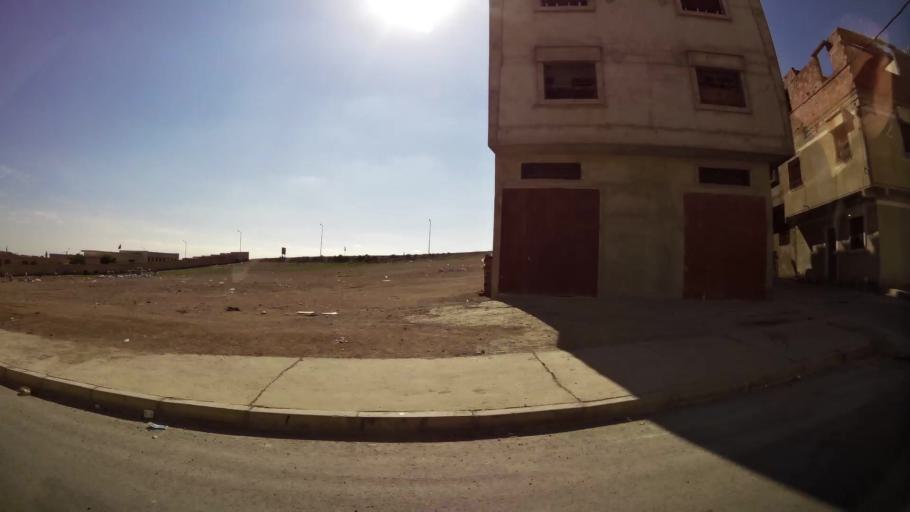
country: MA
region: Oriental
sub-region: Oujda-Angad
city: Oujda
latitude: 34.6479
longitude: -1.9435
